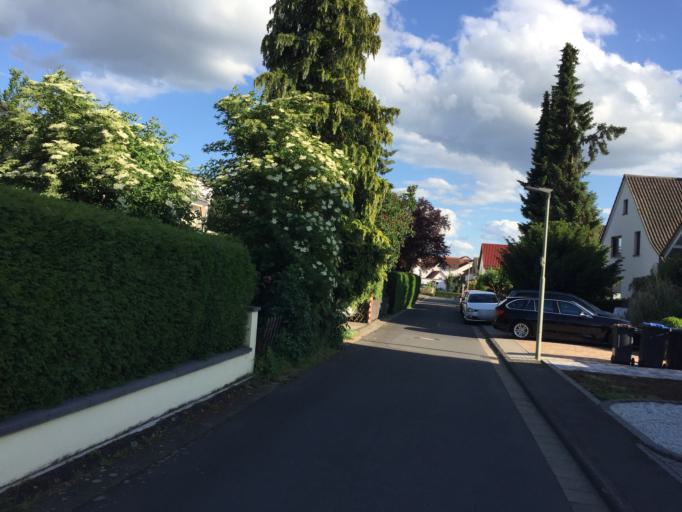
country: DE
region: Hesse
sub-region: Regierungsbezirk Darmstadt
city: Karben
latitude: 50.2248
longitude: 8.7770
